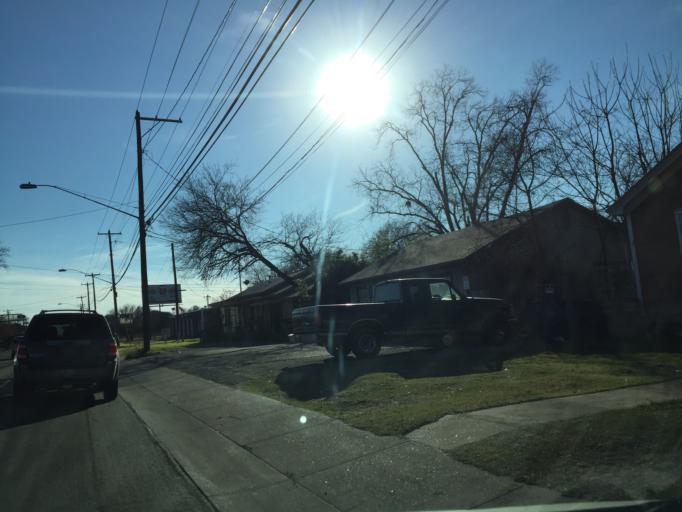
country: US
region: Texas
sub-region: Travis County
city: Austin
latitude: 30.2241
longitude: -97.7711
